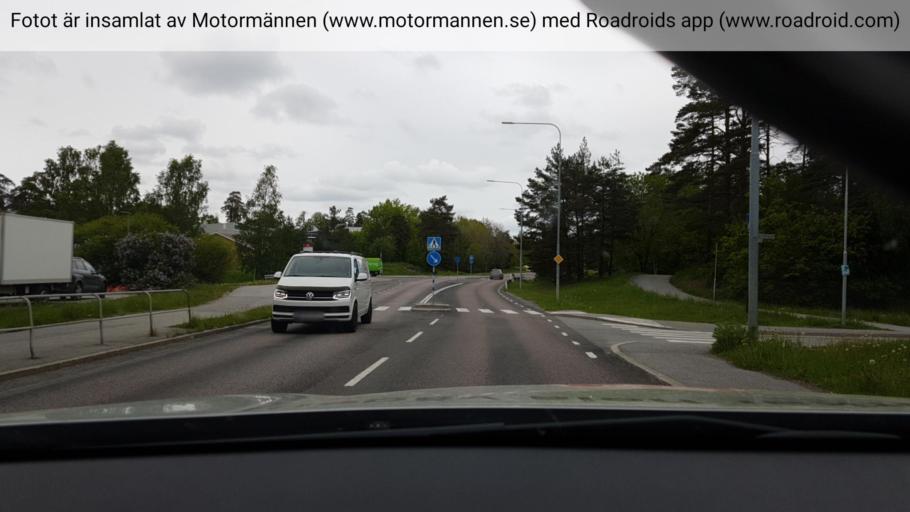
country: SE
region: Stockholm
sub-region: Lidingo
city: Brevik
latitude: 59.3534
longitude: 18.1661
